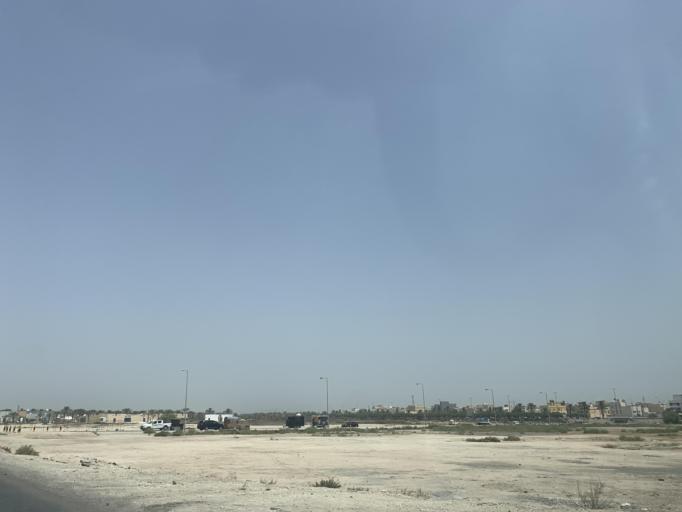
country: BH
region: Central Governorate
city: Madinat Hamad
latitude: 26.1499
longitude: 50.5059
